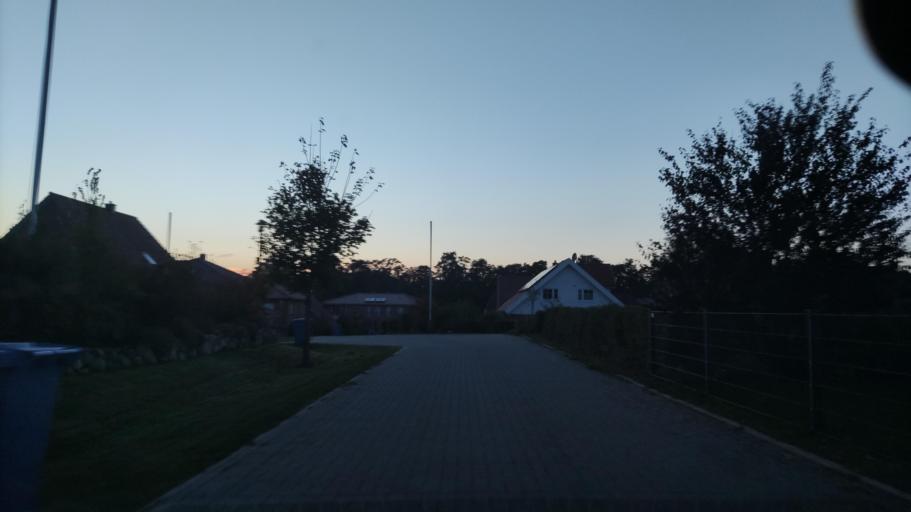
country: DE
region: Lower Saxony
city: Egestorf
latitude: 53.1978
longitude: 10.0680
